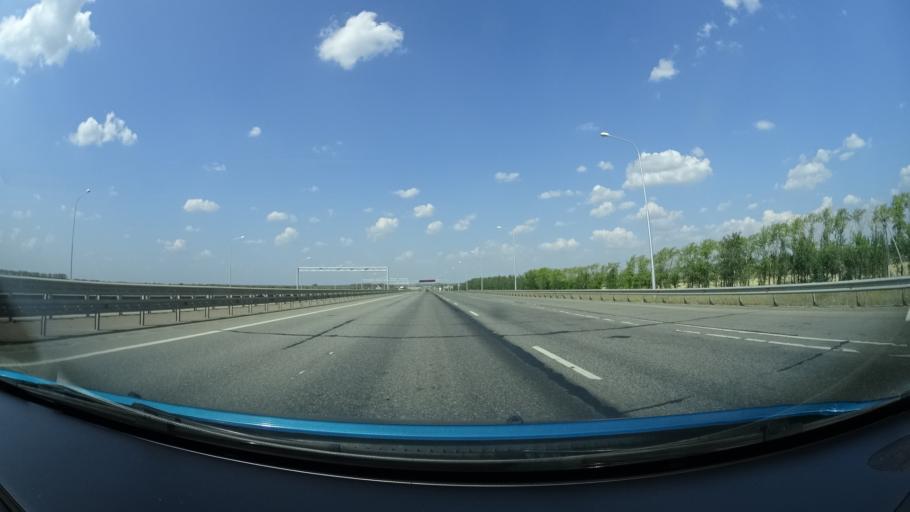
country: RU
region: Bashkortostan
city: Chishmy
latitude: 54.6693
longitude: 55.3958
